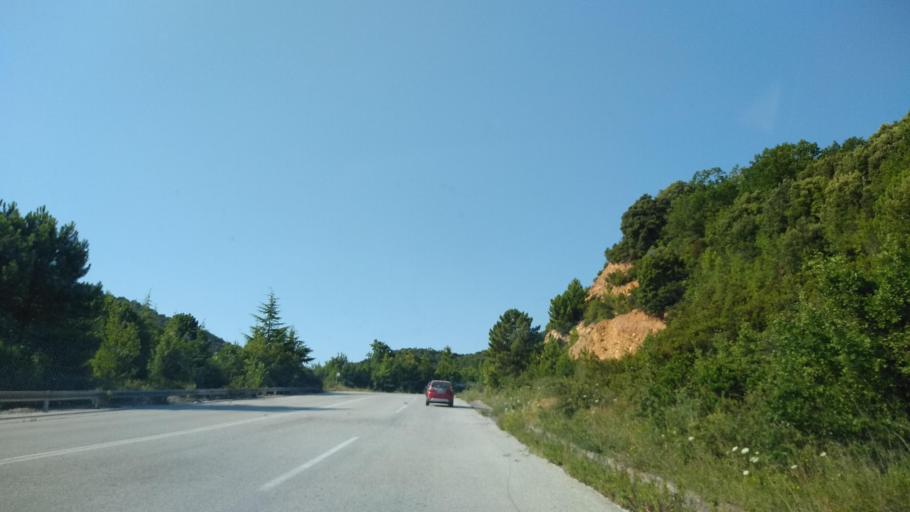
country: GR
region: Central Macedonia
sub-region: Nomos Chalkidikis
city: Stratonion
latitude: 40.5400
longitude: 23.8295
